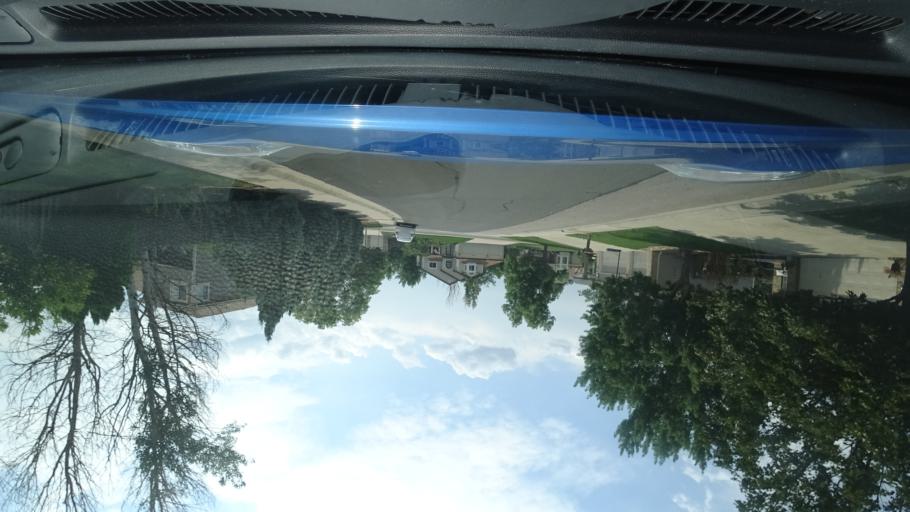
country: US
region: Colorado
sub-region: Adams County
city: Aurora
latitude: 39.6731
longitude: -104.7750
